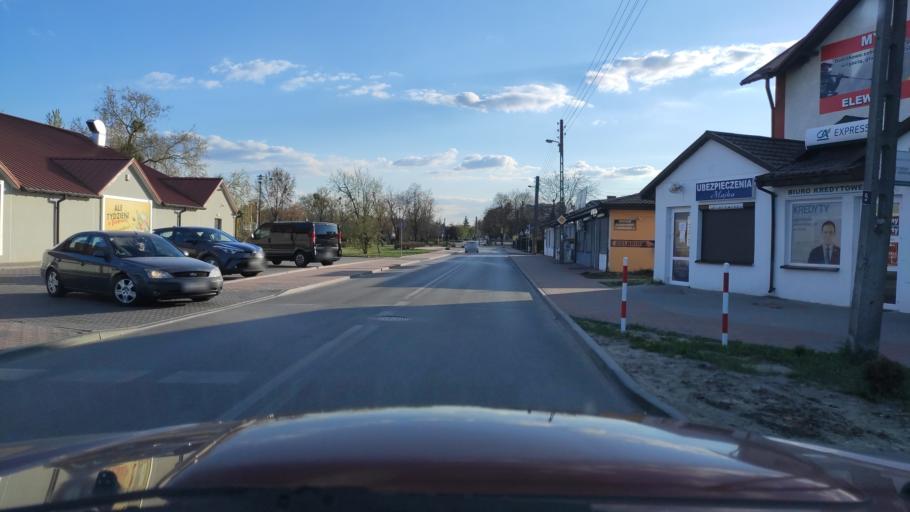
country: PL
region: Masovian Voivodeship
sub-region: Powiat radomski
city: Pionki
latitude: 51.4741
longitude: 21.4439
